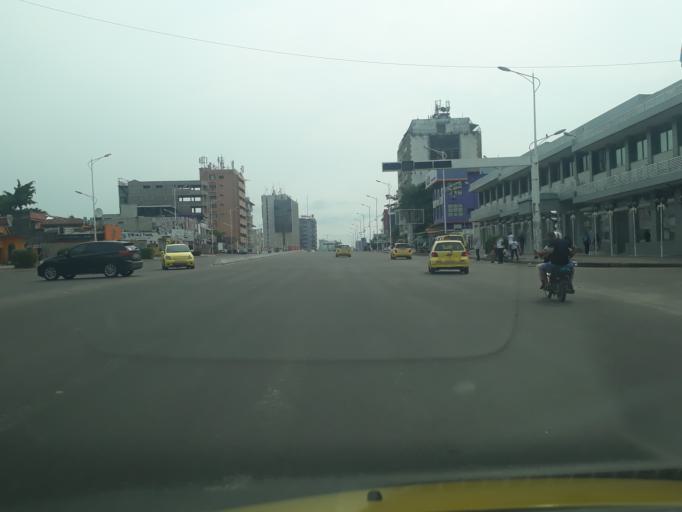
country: CD
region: Kinshasa
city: Kinshasa
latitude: -4.3046
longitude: 15.3055
